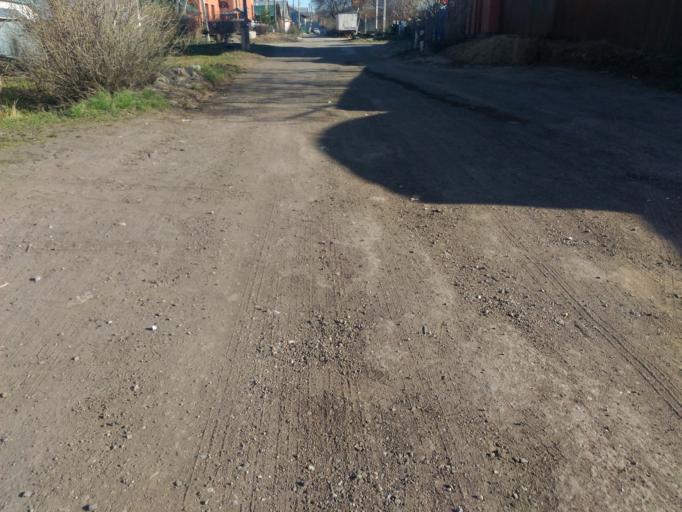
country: RU
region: Ulyanovsk
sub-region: Ulyanovskiy Rayon
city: Ulyanovsk
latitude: 54.3379
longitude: 48.3891
